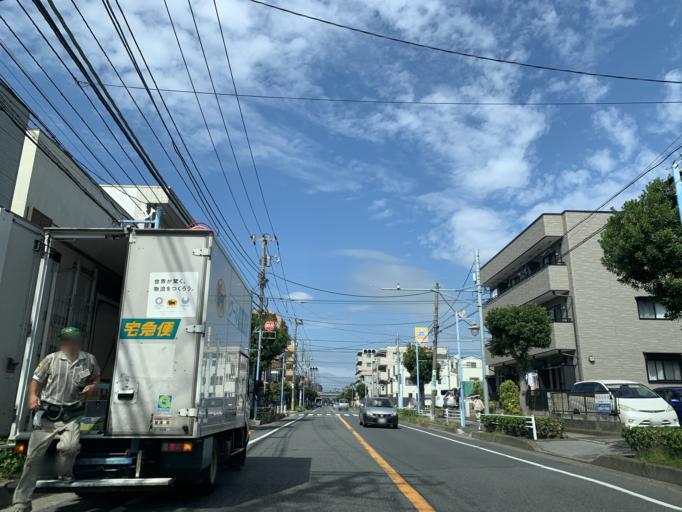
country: JP
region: Tokyo
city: Urayasu
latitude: 35.6865
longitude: 139.9244
